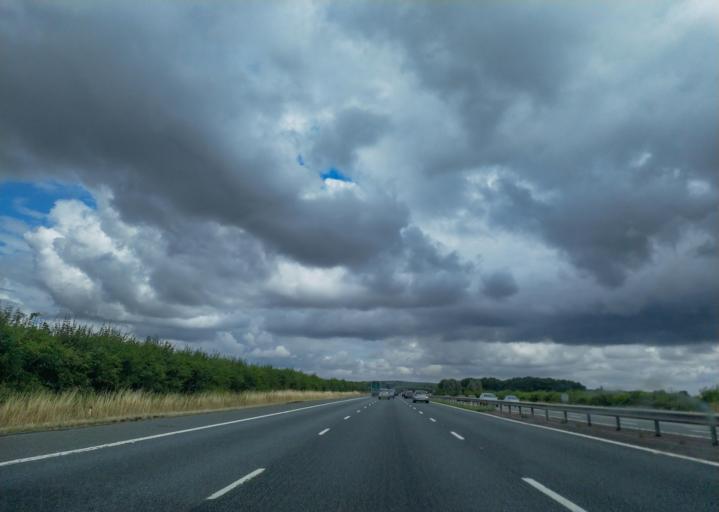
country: GB
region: England
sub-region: Oxfordshire
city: Wheatley
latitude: 51.7697
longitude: -1.1021
